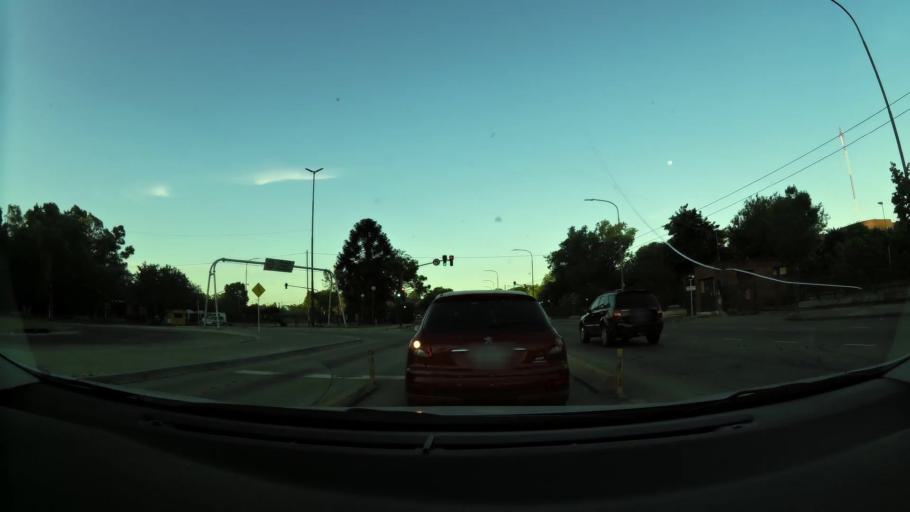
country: AR
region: Buenos Aires F.D.
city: Villa Lugano
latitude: -34.6860
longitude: -58.4567
